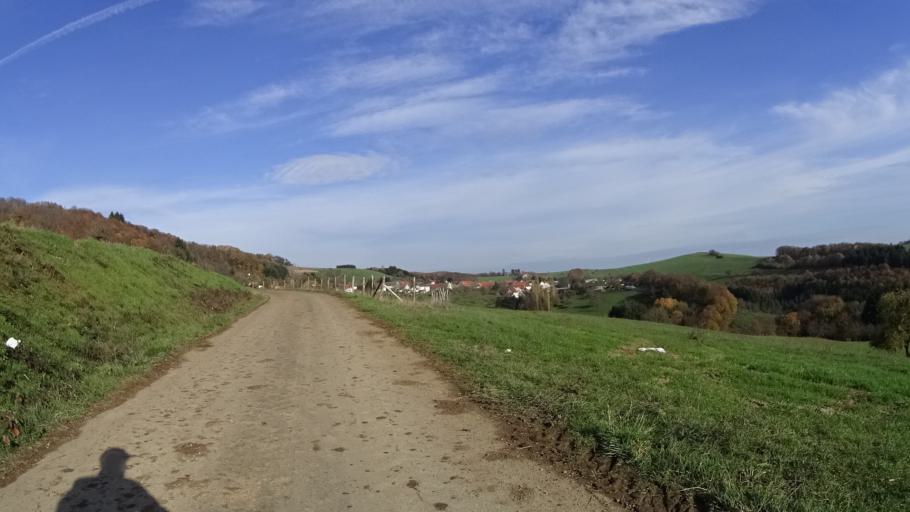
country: DE
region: Rheinland-Pfalz
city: Kirrweiler
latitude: 49.6292
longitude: 7.4948
